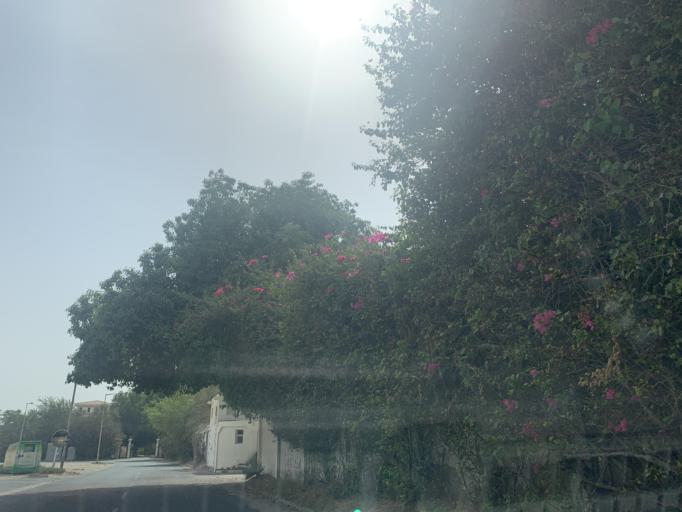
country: BH
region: Manama
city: Jidd Hafs
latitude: 26.2032
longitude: 50.4784
